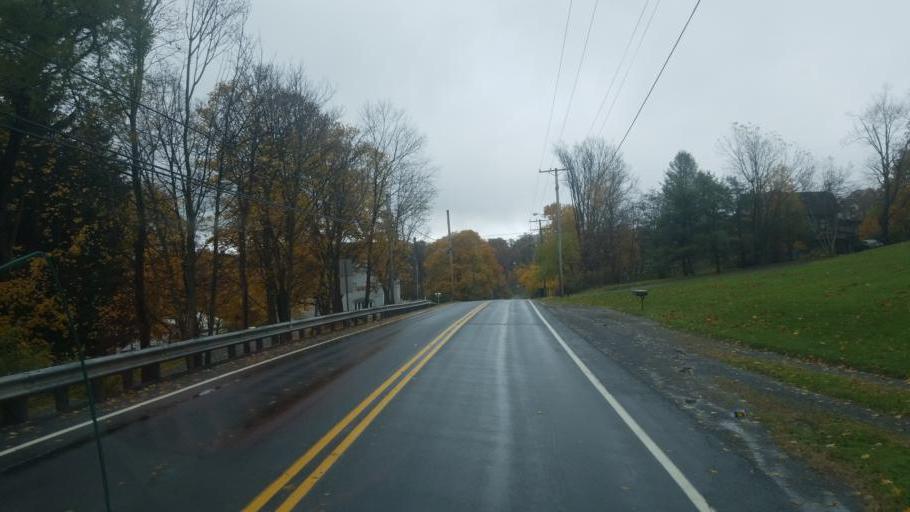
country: US
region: Pennsylvania
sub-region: Centre County
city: Milesburg
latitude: 41.0292
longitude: -77.9548
